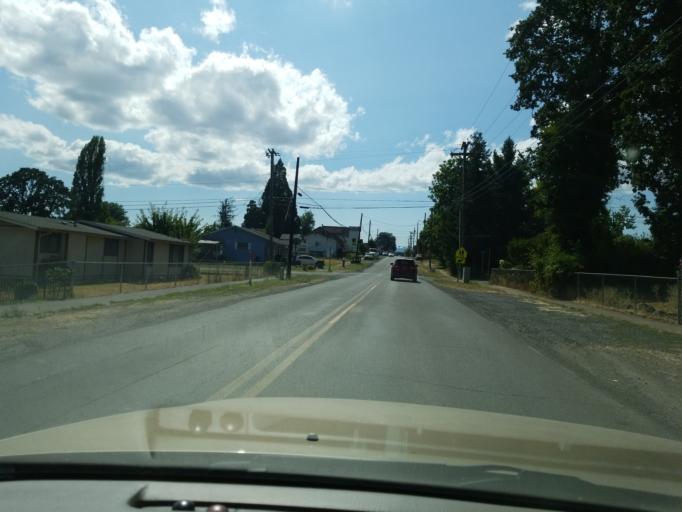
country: US
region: Oregon
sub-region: Yamhill County
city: Carlton
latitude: 45.2942
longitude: -123.1729
